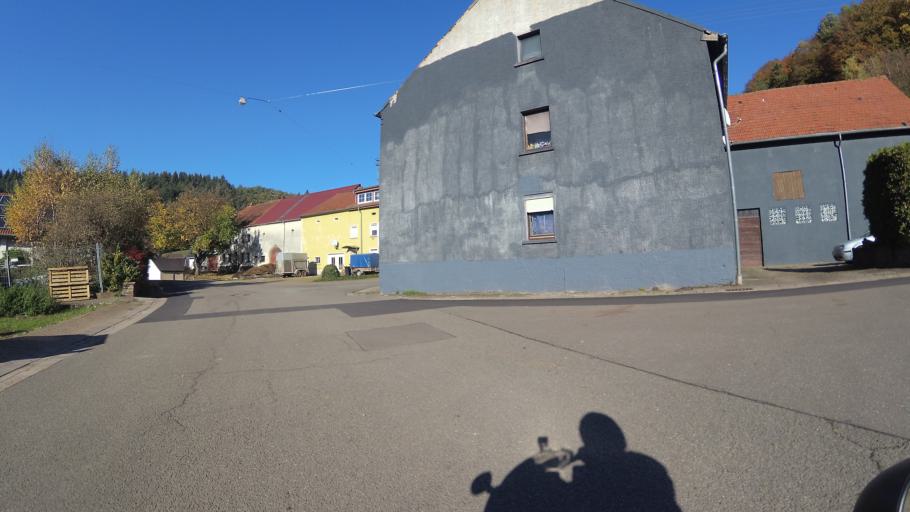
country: DE
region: Saarland
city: Losheim
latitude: 49.4731
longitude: 6.7244
